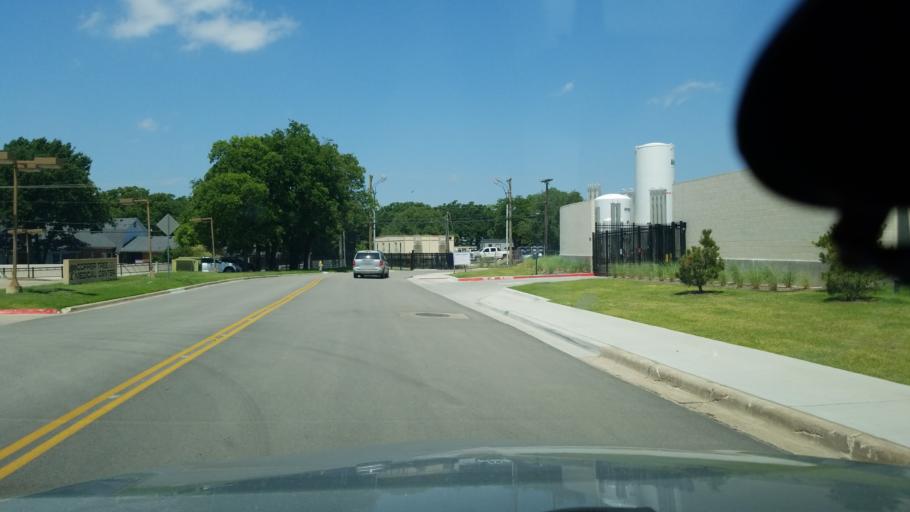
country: US
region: Texas
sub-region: Dallas County
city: Irving
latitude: 32.8337
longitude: -96.9620
